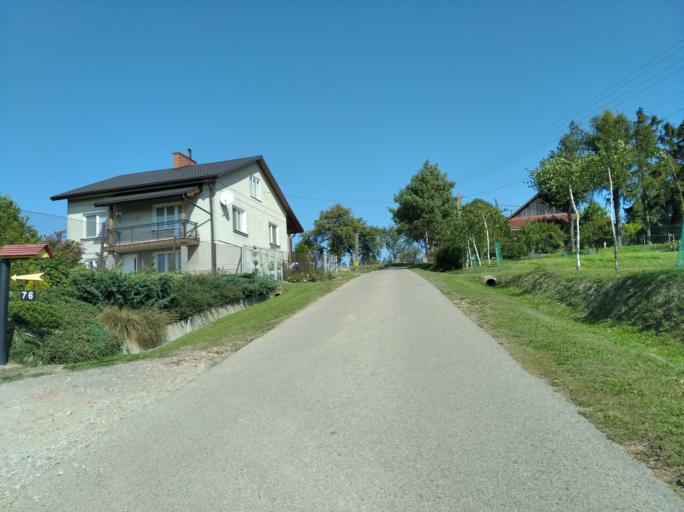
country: PL
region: Subcarpathian Voivodeship
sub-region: Powiat strzyzowski
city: Czudec
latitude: 49.9666
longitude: 21.8113
